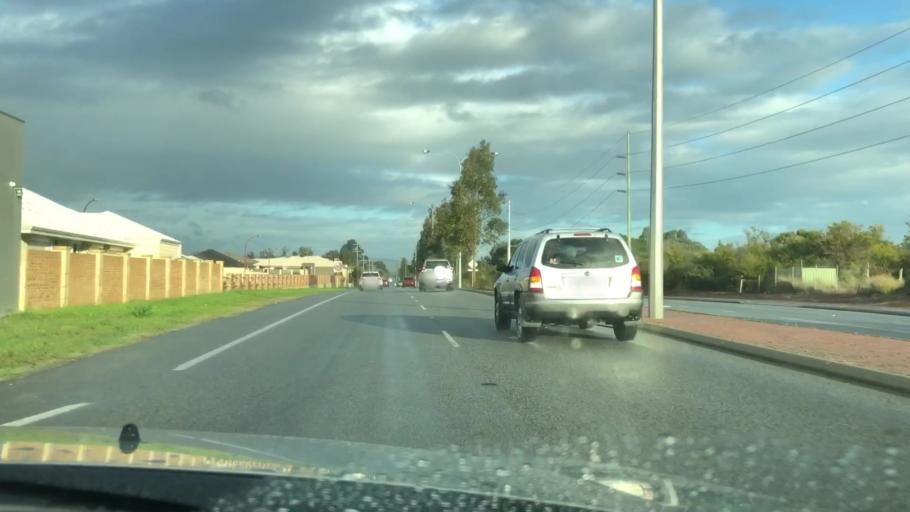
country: AU
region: Western Australia
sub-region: Armadale
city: Harrisdale
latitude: -32.1084
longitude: 115.9399
